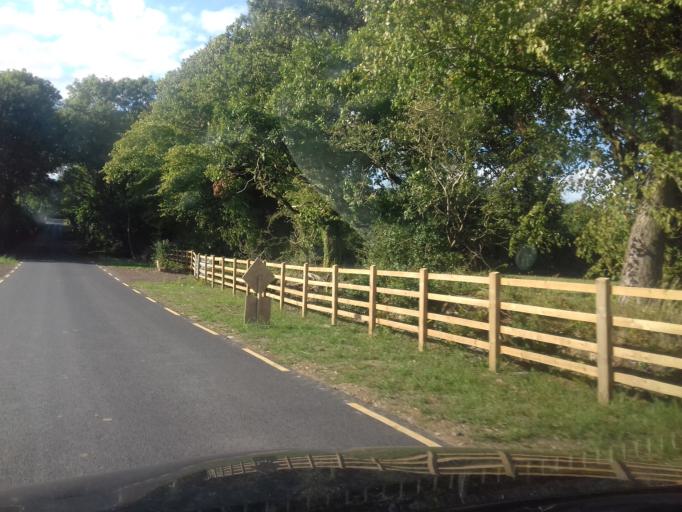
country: IE
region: Leinster
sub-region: Loch Garman
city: New Ross
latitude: 52.3746
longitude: -6.9213
